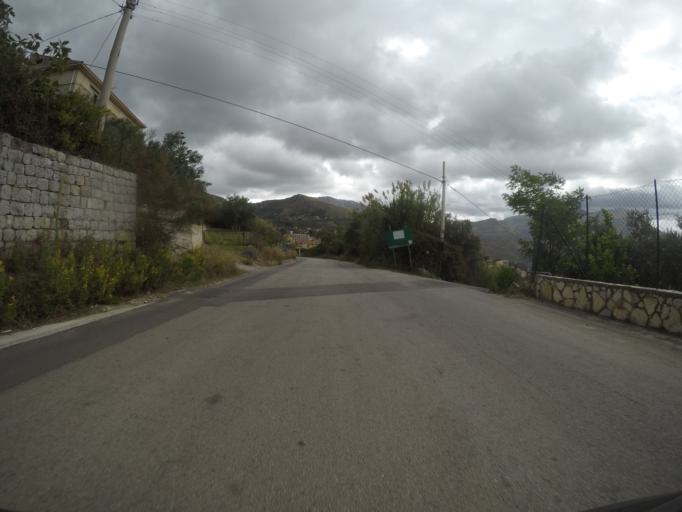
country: IT
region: Sicily
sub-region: Palermo
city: Montelepre
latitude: 38.0942
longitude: 13.1724
